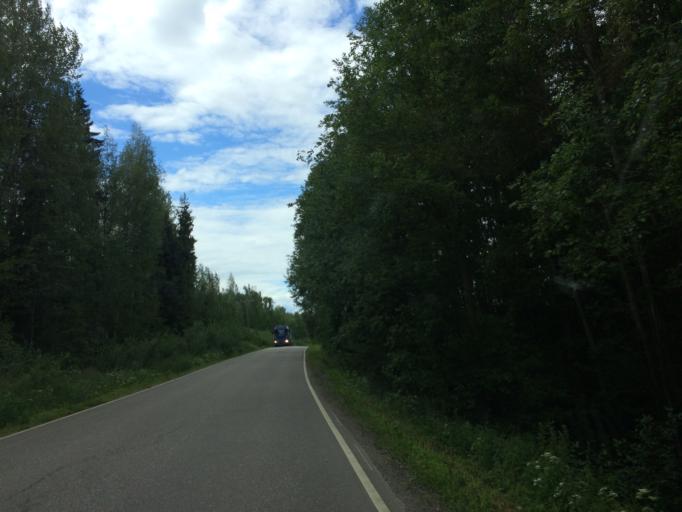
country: FI
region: Haeme
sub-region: Haemeenlinna
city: Tervakoski
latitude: 60.8299
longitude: 24.5976
